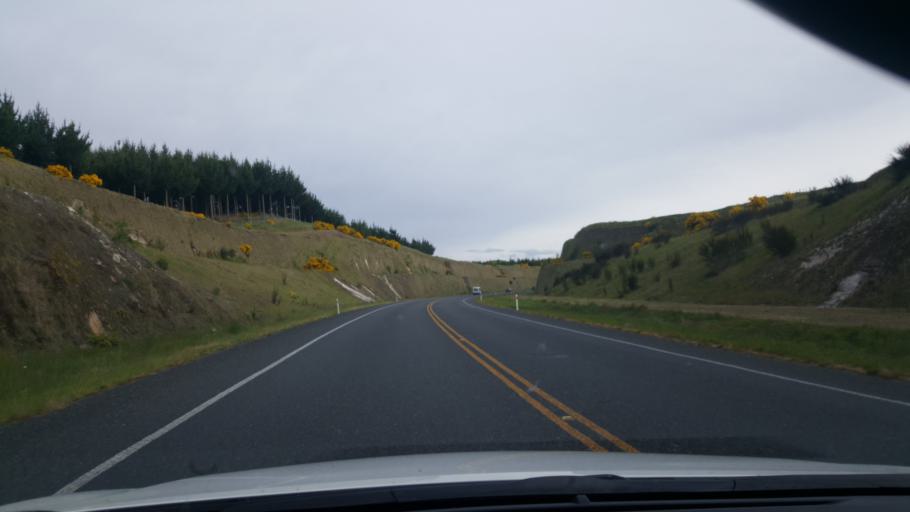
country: NZ
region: Waikato
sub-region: Taupo District
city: Taupo
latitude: -38.6723
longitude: 176.1144
